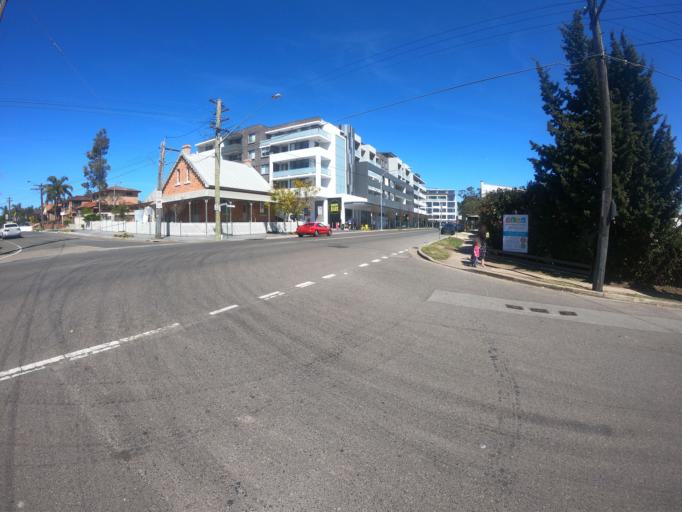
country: AU
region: New South Wales
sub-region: Hunters Hill
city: Gladesville
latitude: -33.8229
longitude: 151.1246
